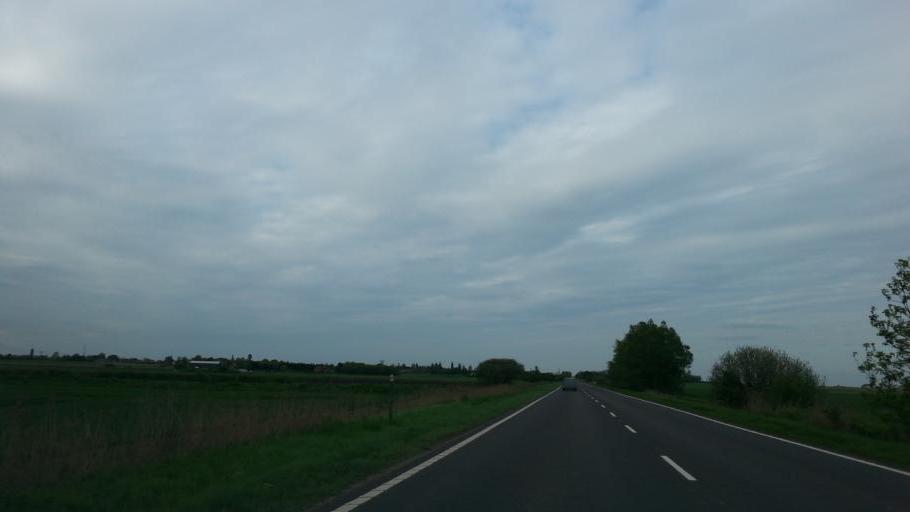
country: GB
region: England
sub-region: Cambridgeshire
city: Doddington
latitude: 52.4797
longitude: 0.0577
